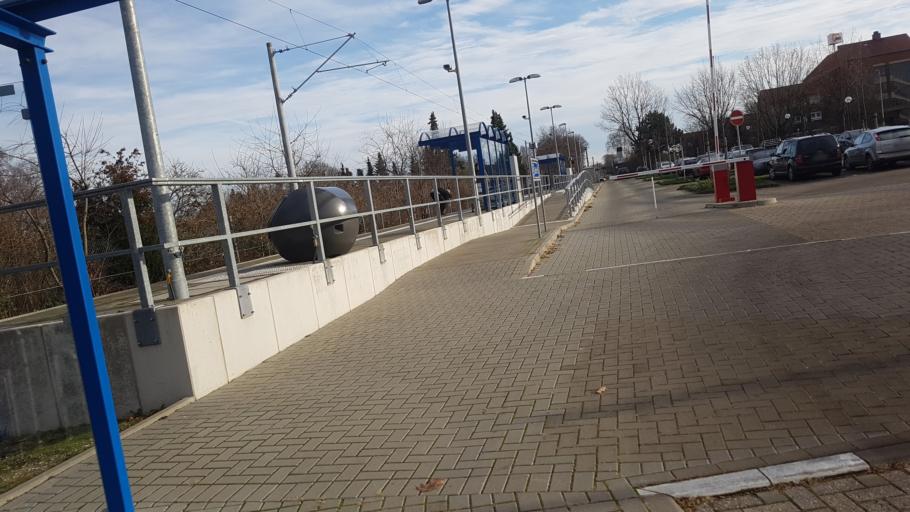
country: DE
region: North Rhine-Westphalia
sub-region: Regierungsbezirk Koln
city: Heinsberg
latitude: 51.0620
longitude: 6.1080
